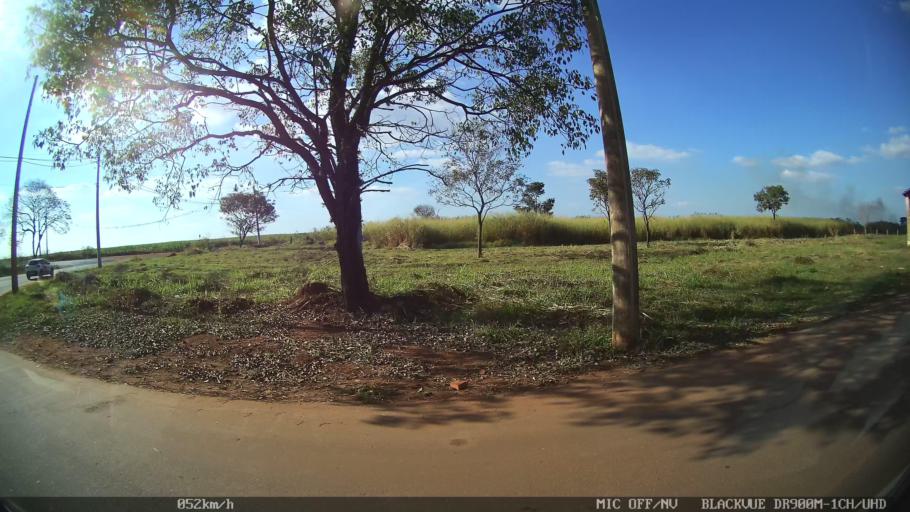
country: BR
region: Sao Paulo
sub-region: Americana
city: Americana
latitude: -22.7849
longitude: -47.3592
